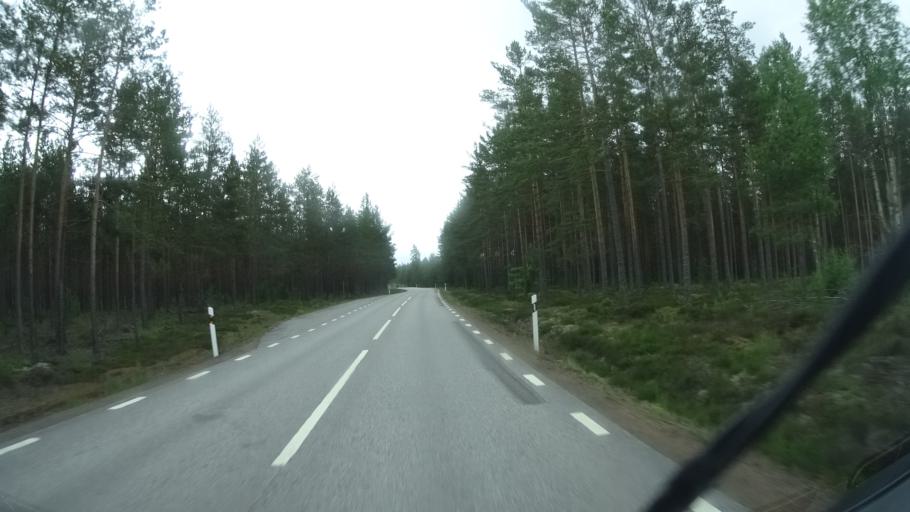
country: SE
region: Kalmar
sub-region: Hultsfreds Kommun
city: Hultsfred
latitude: 57.5255
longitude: 15.7957
